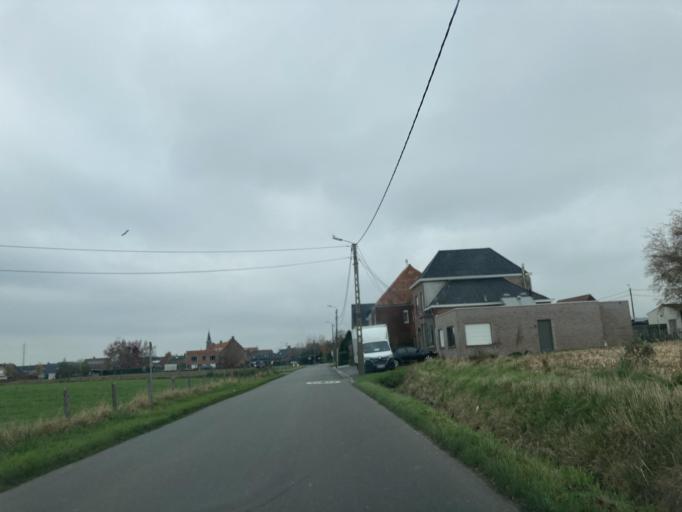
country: BE
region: Flanders
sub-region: Provincie West-Vlaanderen
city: Lendelede
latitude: 50.8676
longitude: 3.2444
